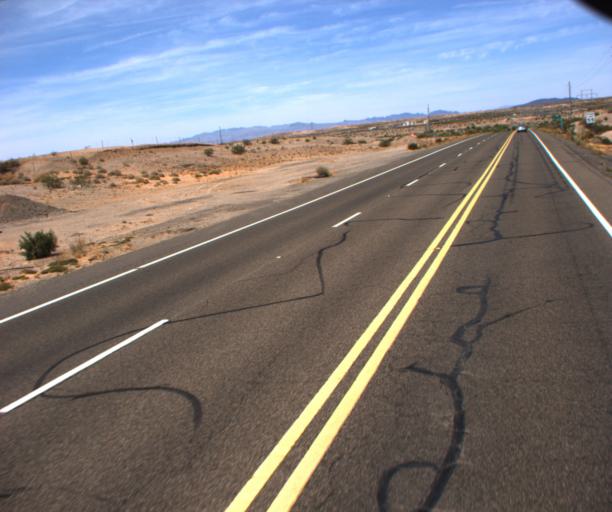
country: US
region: Arizona
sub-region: La Paz County
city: Parker
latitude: 33.9839
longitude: -114.2169
